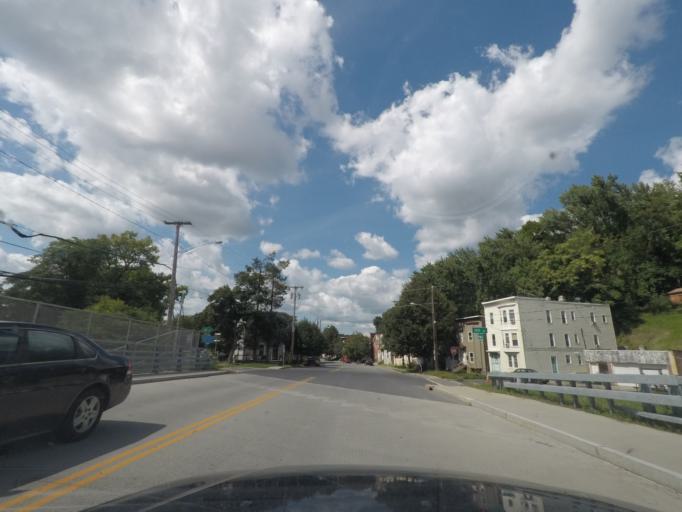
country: US
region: New York
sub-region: Rensselaer County
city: Troy
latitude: 42.7195
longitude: -73.6850
